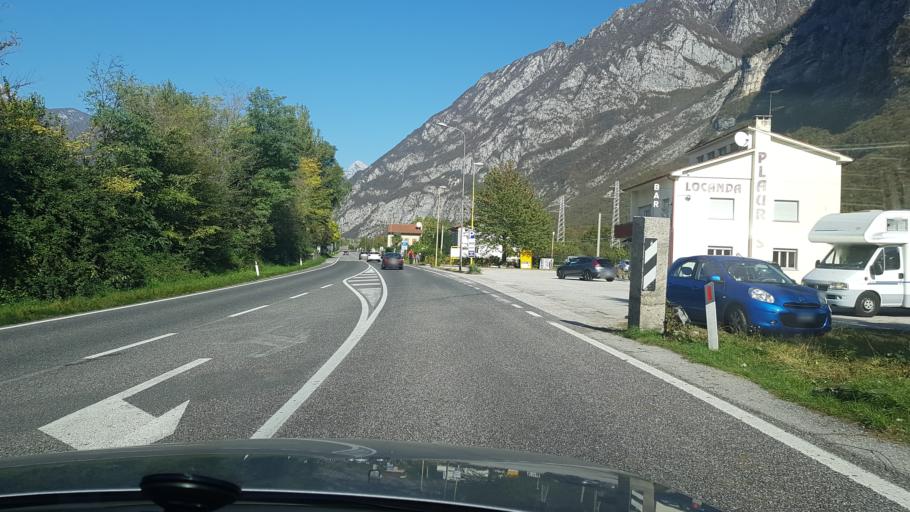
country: IT
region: Friuli Venezia Giulia
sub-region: Provincia di Udine
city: Venzone
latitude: 46.3388
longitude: 13.1398
